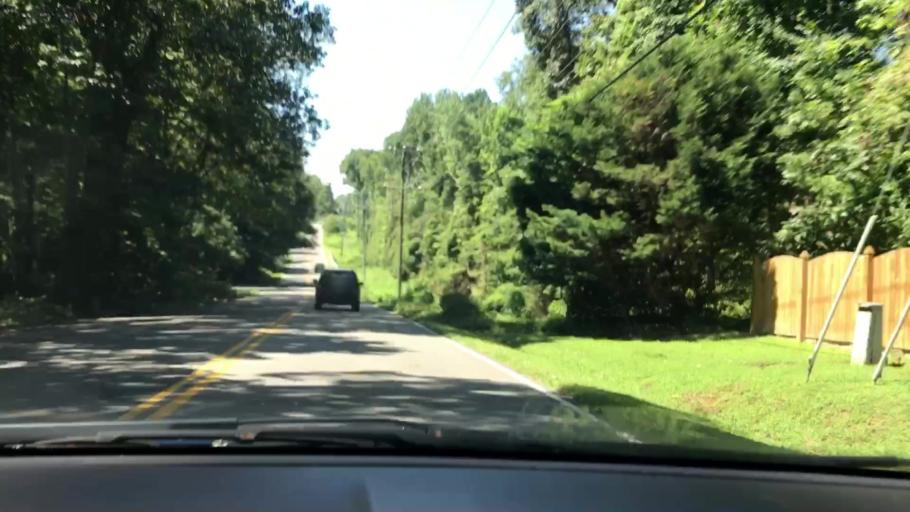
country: US
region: Virginia
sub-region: Henrico County
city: Short Pump
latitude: 37.6073
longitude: -77.5989
